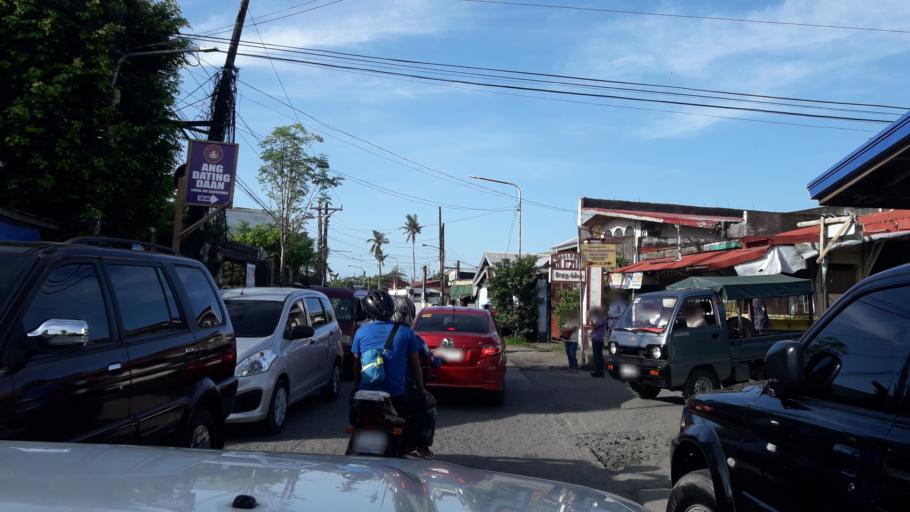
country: PH
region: Eastern Visayas
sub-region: Province of Leyte
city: Panalanoy
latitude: 11.2196
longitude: 125.0033
